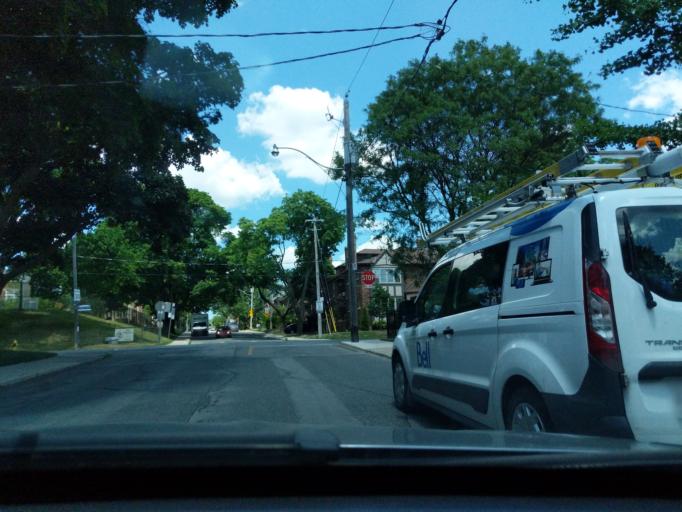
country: CA
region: Ontario
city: Toronto
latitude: 43.7013
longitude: -79.4085
